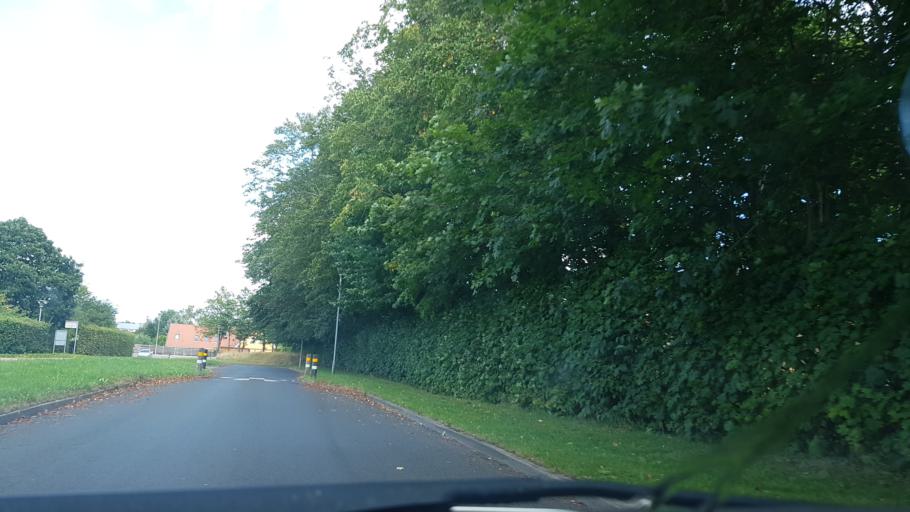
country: DK
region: Capital Region
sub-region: Fredensborg Kommune
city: Humlebaek
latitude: 55.9861
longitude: 12.5321
